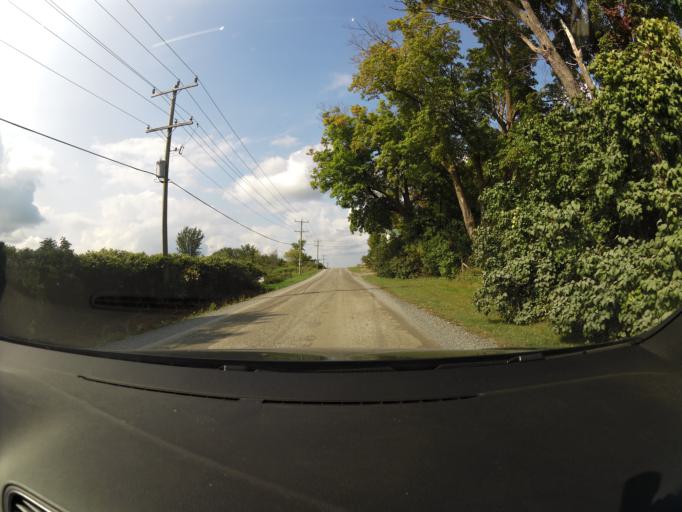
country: CA
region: Ontario
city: Arnprior
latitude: 45.4158
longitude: -76.2438
